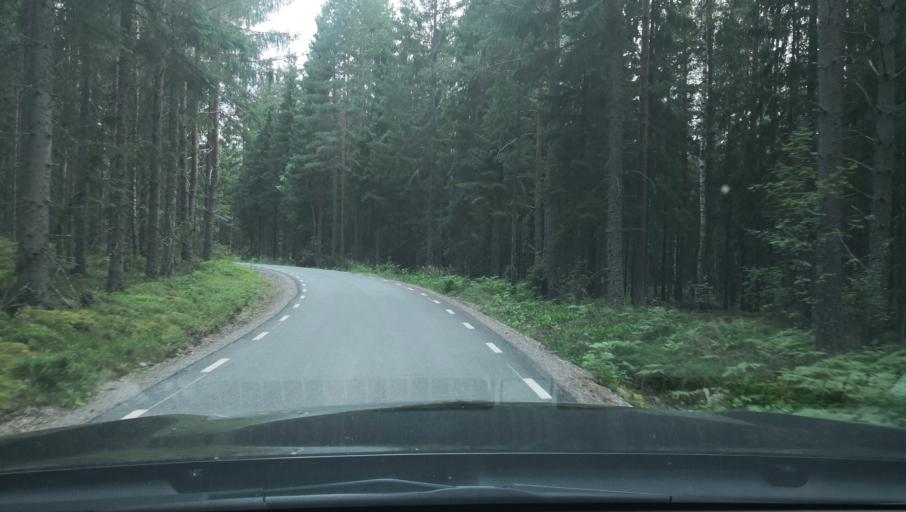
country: SE
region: Vaestmanland
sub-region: Surahammars Kommun
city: Surahammar
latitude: 59.6604
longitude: 16.1320
